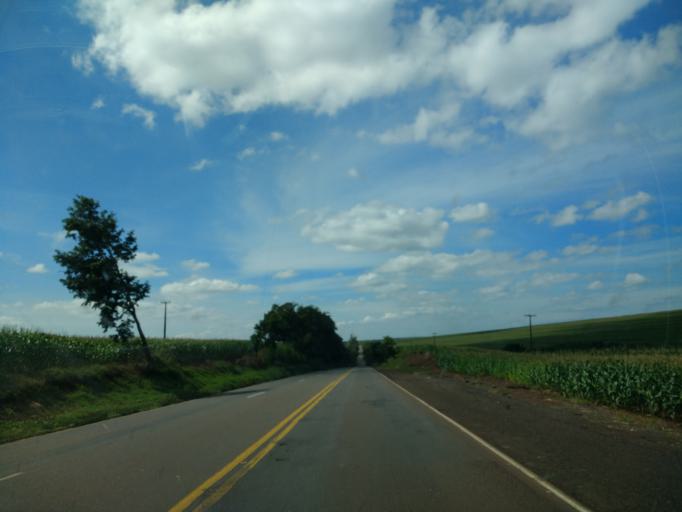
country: BR
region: Parana
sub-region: Terra Boa
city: Terra Boa
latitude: -23.5996
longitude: -52.3969
